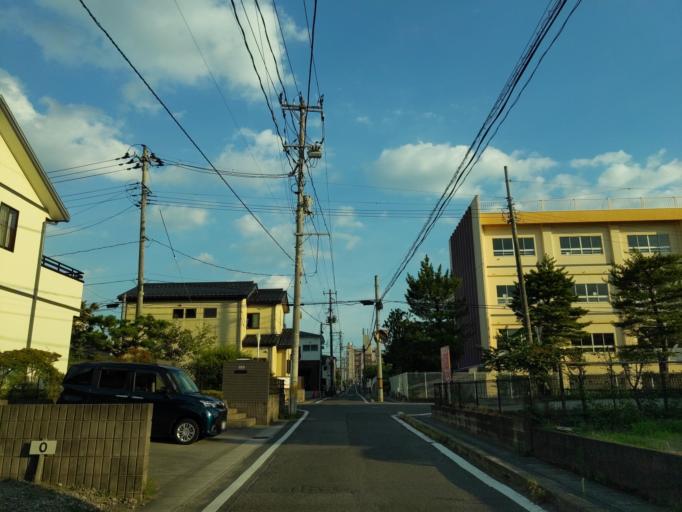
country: JP
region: Fukushima
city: Koriyama
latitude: 37.3948
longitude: 140.3515
